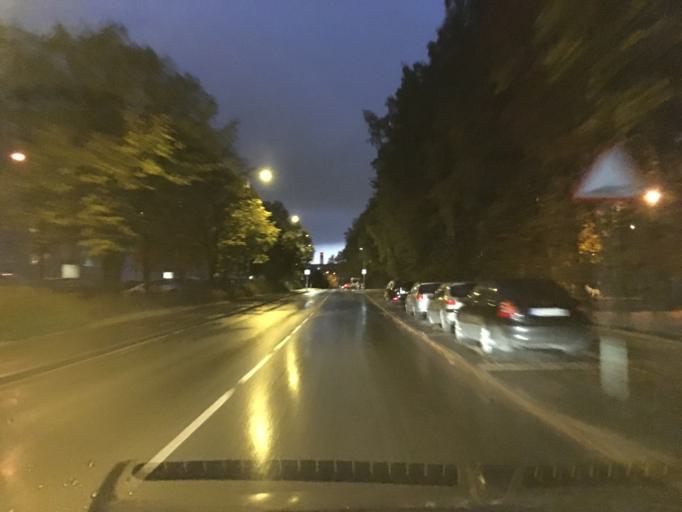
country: EE
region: Harju
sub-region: Tallinna linn
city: Tallinn
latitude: 59.4333
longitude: 24.7972
